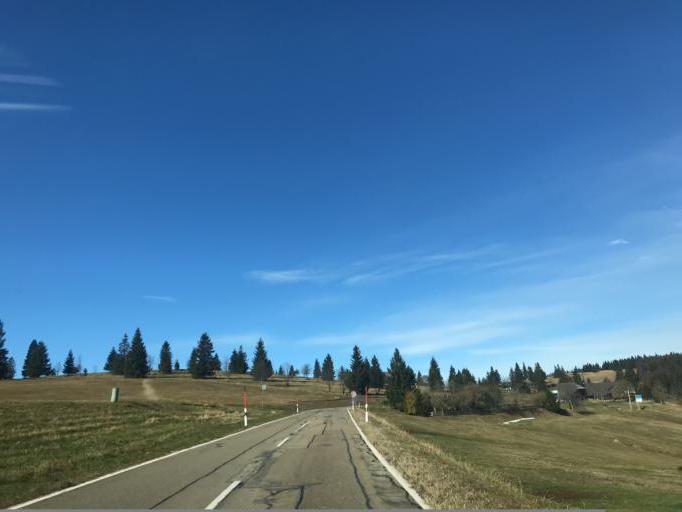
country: DE
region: Baden-Wuerttemberg
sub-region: Freiburg Region
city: Sankt Peter
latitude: 48.0603
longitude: 8.0186
